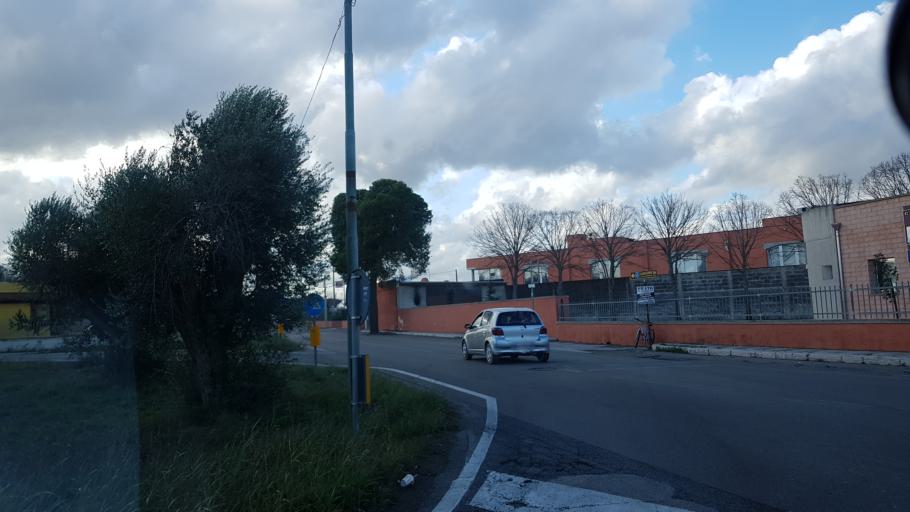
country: IT
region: Apulia
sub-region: Provincia di Brindisi
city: Torchiarolo
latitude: 40.4866
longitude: 18.0442
